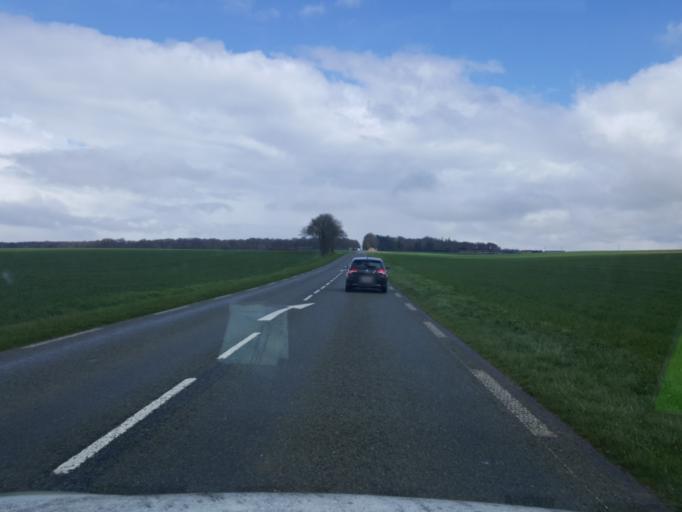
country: FR
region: Picardie
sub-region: Departement de l'Oise
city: Chaumont-en-Vexin
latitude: 49.3369
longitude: 1.9154
